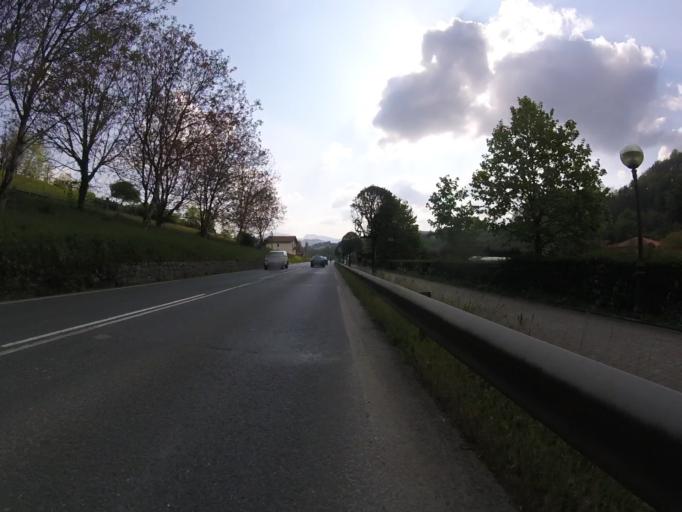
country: ES
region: Basque Country
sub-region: Provincia de Guipuzcoa
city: Azkoitia
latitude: 43.1745
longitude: -2.2939
